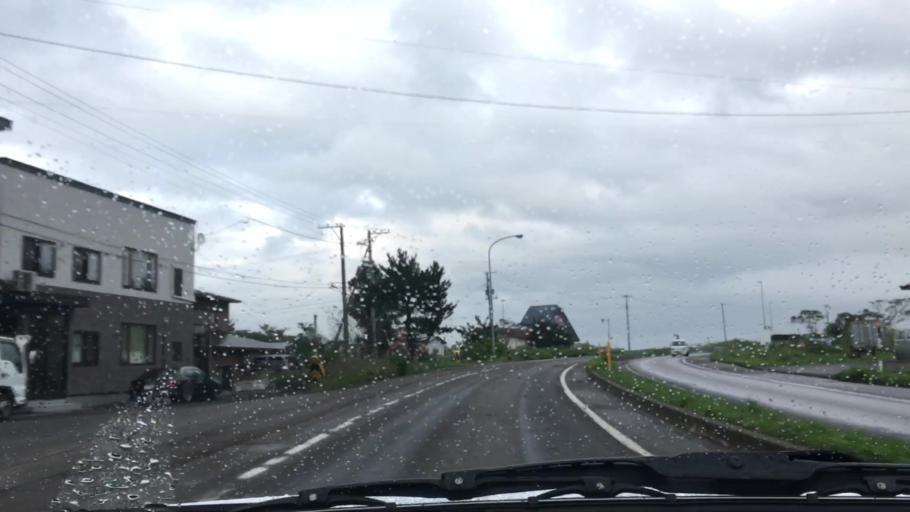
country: JP
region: Hokkaido
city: Nanae
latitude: 42.1885
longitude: 140.4334
